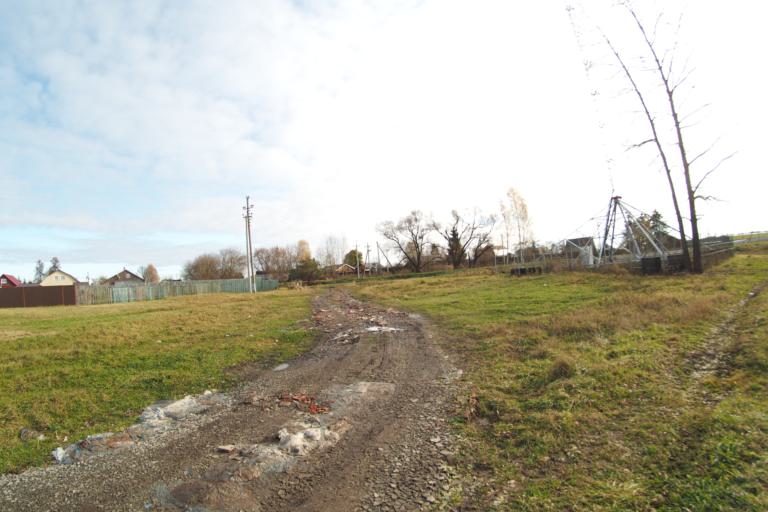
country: RU
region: Moskovskaya
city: Davydovo
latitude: 55.5544
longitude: 38.8058
